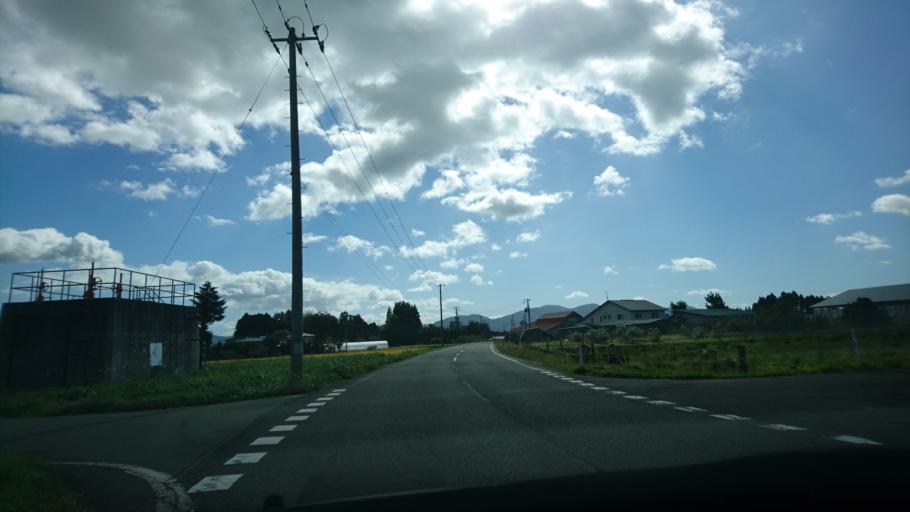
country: JP
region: Iwate
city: Mizusawa
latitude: 39.0785
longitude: 141.1059
